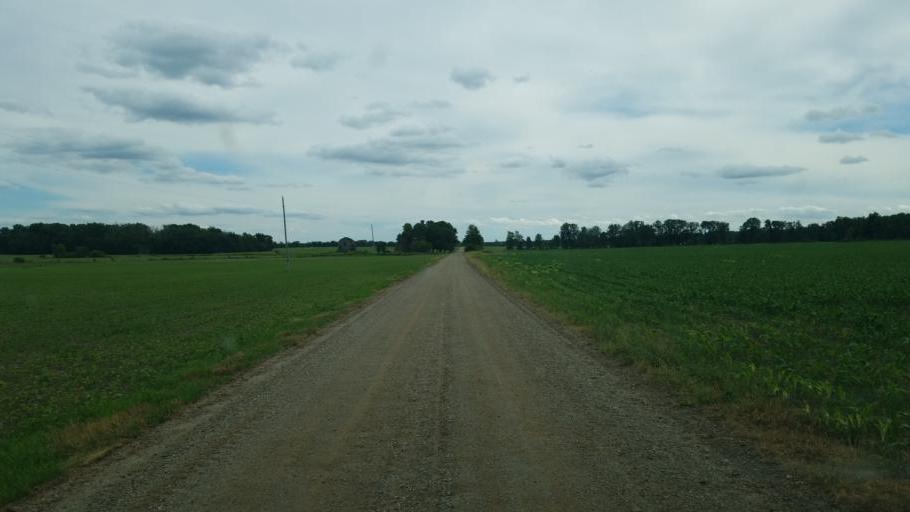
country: US
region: Michigan
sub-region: Barry County
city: Nashville
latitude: 42.6677
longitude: -84.9755
